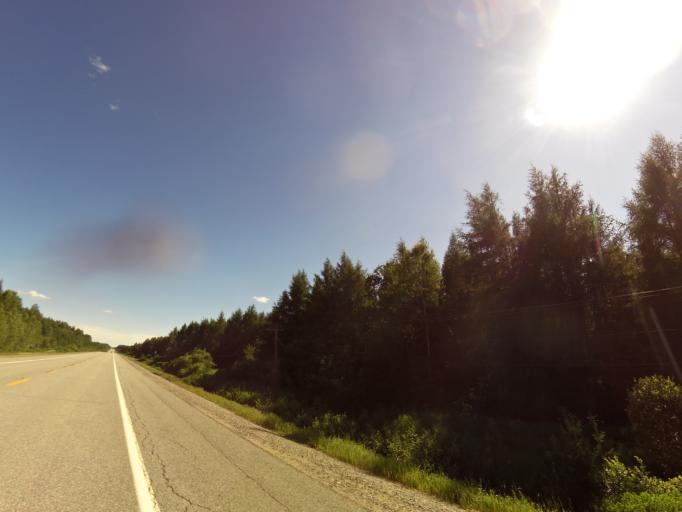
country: CA
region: Quebec
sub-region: Abitibi-Temiscamingue
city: Senneterre
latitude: 47.9843
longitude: -77.3608
